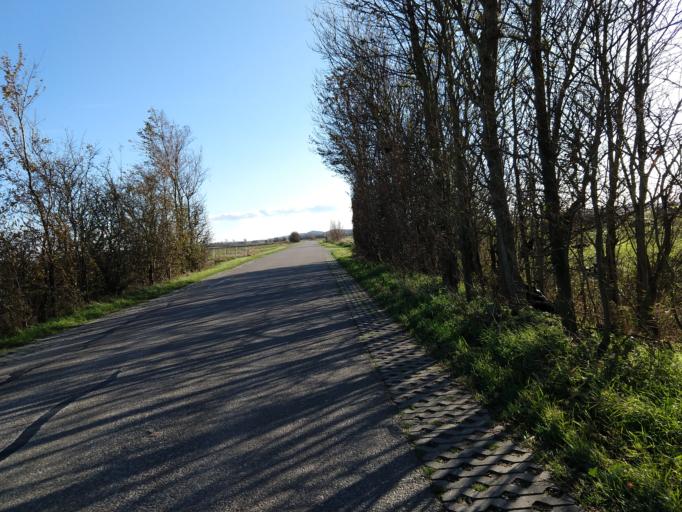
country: NL
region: Zeeland
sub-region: Gemeente Vlissingen
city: Vlissingen
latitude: 51.5232
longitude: 3.4842
